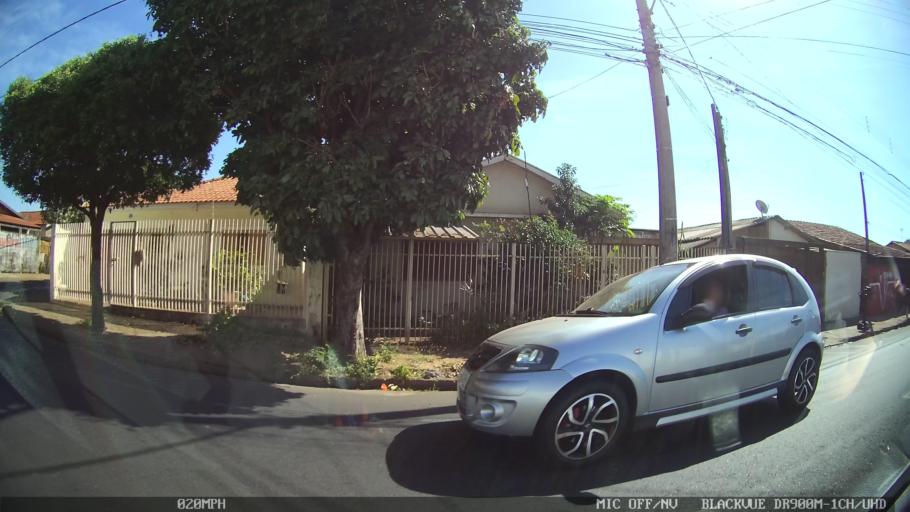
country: BR
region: Sao Paulo
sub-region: Sao Jose Do Rio Preto
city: Sao Jose do Rio Preto
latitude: -20.7758
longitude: -49.4187
